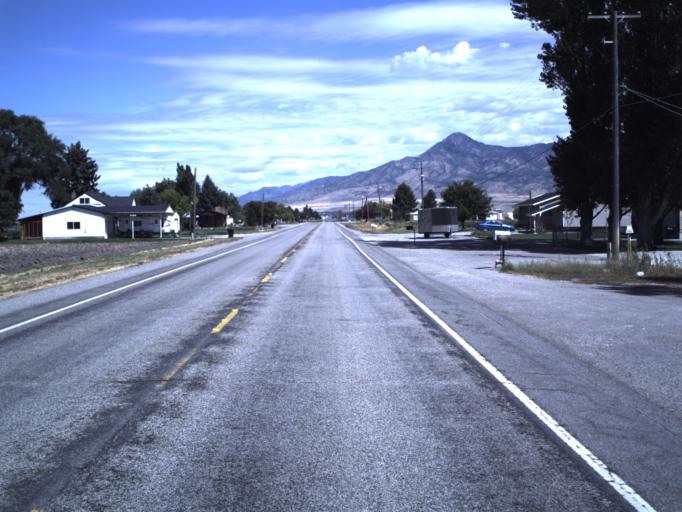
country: US
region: Utah
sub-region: Box Elder County
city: Garland
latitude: 41.8096
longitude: -112.1451
